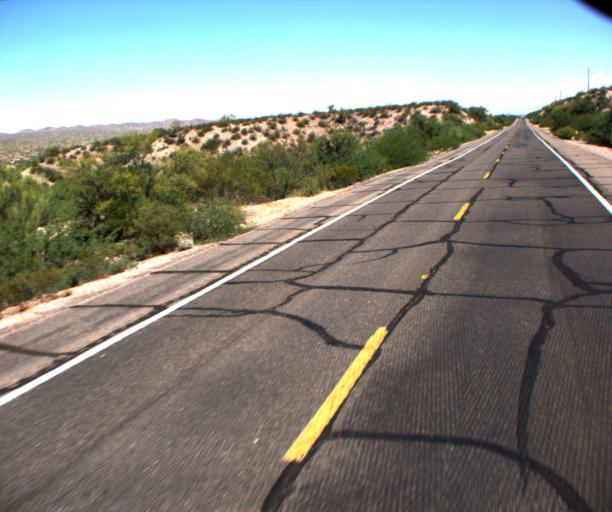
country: US
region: Arizona
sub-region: Pinal County
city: Mammoth
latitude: 32.7680
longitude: -110.6572
